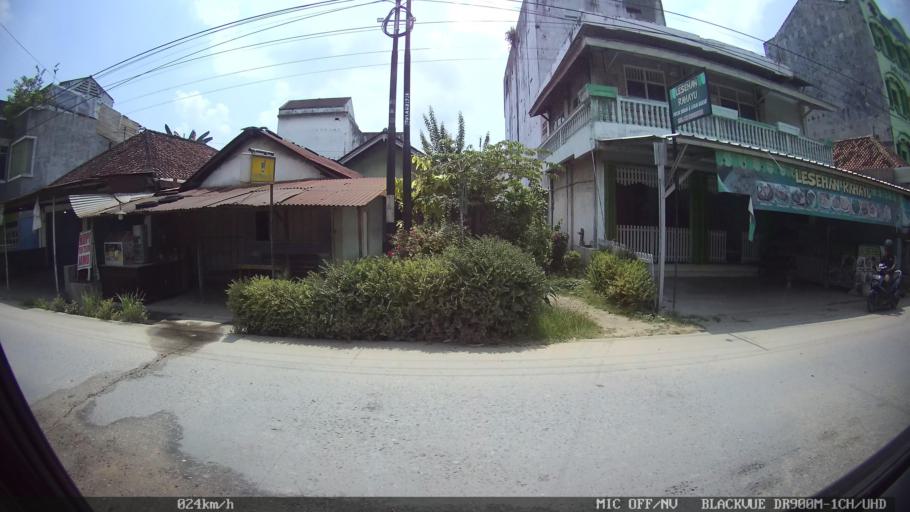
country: ID
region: Lampung
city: Pringsewu
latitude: -5.3539
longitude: 104.9766
